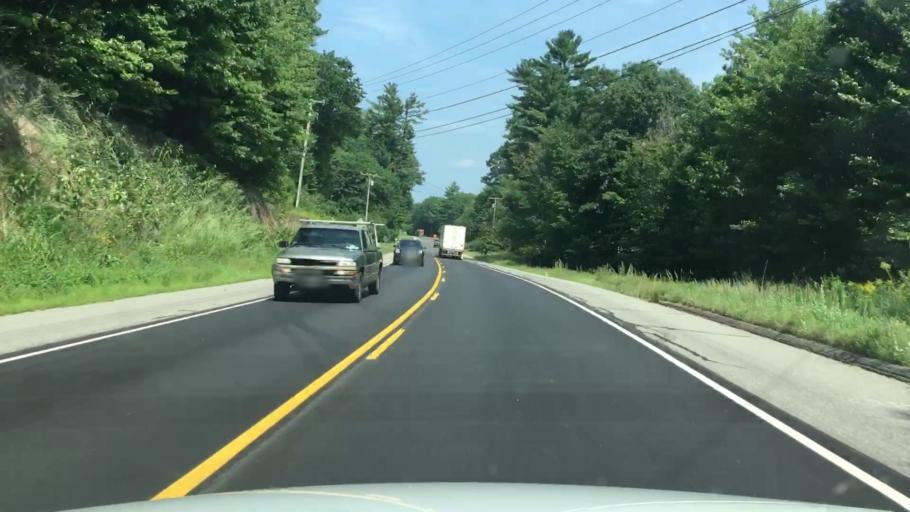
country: US
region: Maine
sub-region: Androscoggin County
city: Turner
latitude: 44.3041
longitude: -70.2674
